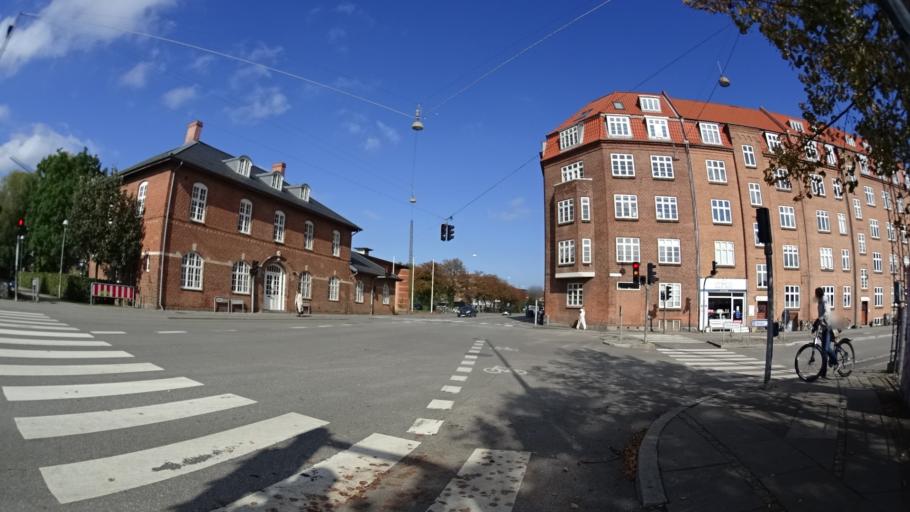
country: DK
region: Central Jutland
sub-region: Arhus Kommune
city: Arhus
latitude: 56.1546
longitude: 10.1936
